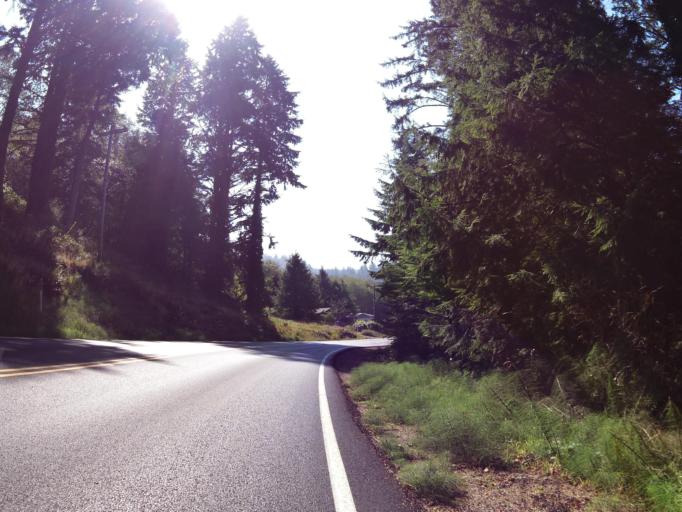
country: US
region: Oregon
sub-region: Tillamook County
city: Pacific City
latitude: 45.2691
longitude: -123.9468
